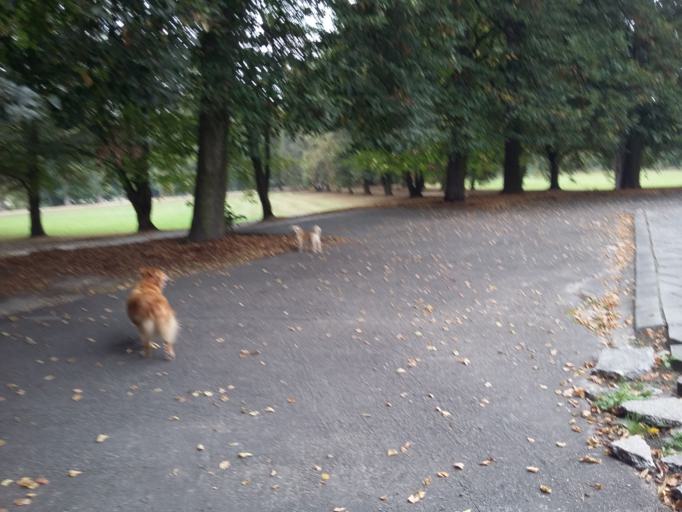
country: PL
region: Lodz Voivodeship
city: Lodz
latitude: 51.7664
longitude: 19.4149
